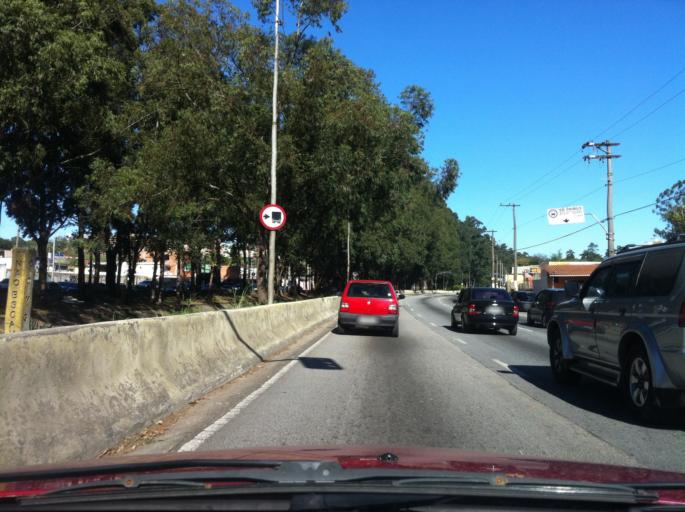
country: BR
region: Sao Paulo
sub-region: Ferraz De Vasconcelos
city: Ferraz de Vasconcelos
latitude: -23.5439
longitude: -46.4479
